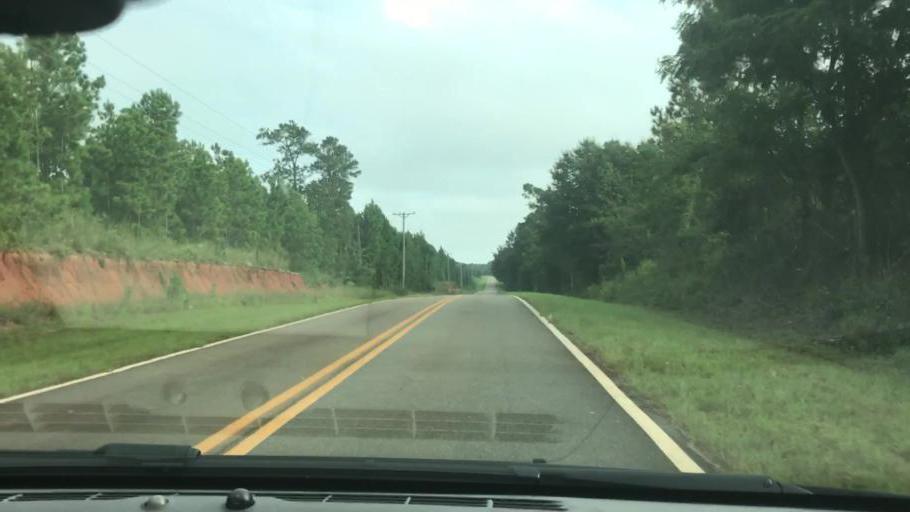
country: US
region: Georgia
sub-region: Stewart County
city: Lumpkin
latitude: 32.0307
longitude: -84.9115
